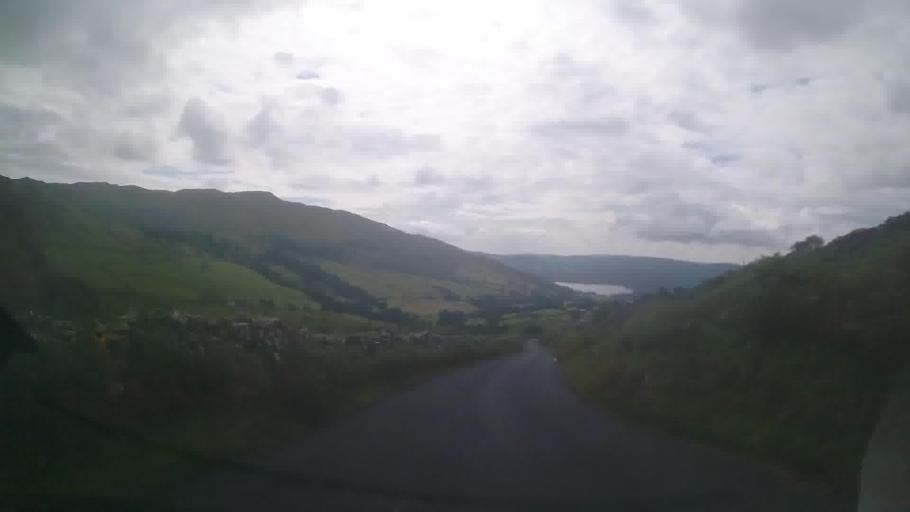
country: GB
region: England
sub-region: Cumbria
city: Ambleside
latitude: 54.4464
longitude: -2.9414
